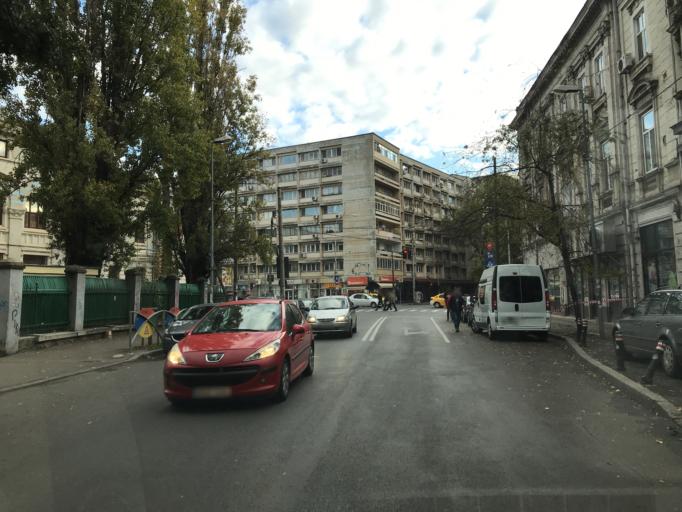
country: RO
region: Bucuresti
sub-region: Municipiul Bucuresti
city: Bucuresti
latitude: 44.4351
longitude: 26.0895
